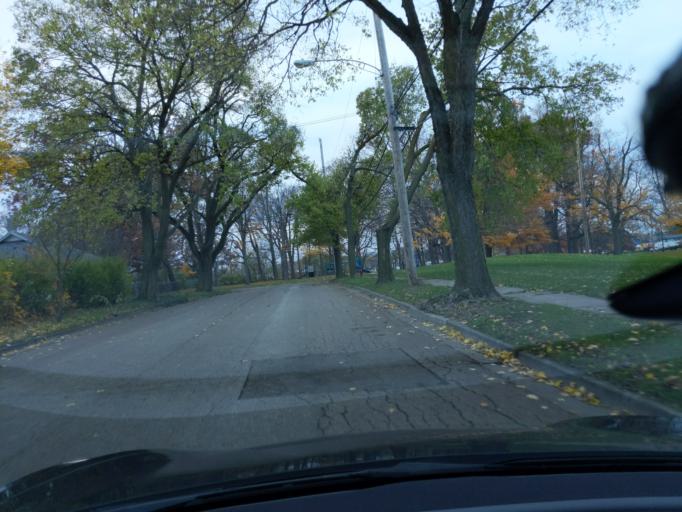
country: US
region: Michigan
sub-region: Ingham County
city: Lansing
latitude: 42.7536
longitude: -84.5530
